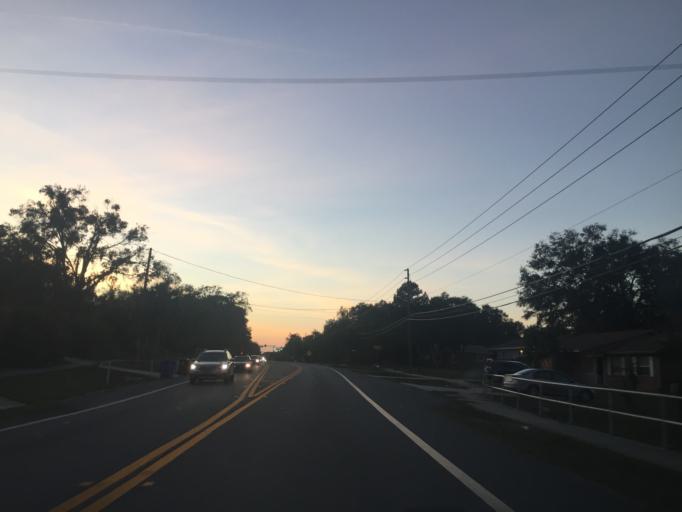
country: US
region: Florida
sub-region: Seminole County
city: Oviedo
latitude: 28.6703
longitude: -81.1927
